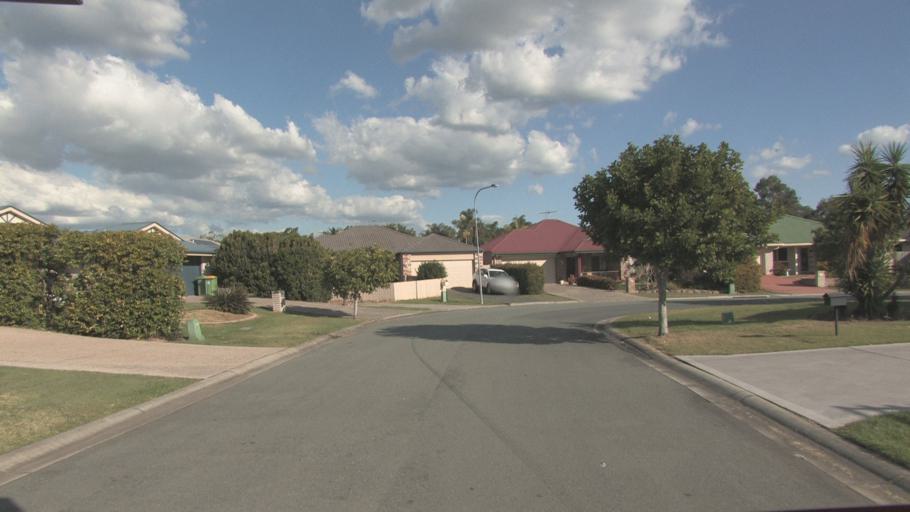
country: AU
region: Queensland
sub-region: Logan
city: Beenleigh
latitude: -27.6884
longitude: 153.1780
